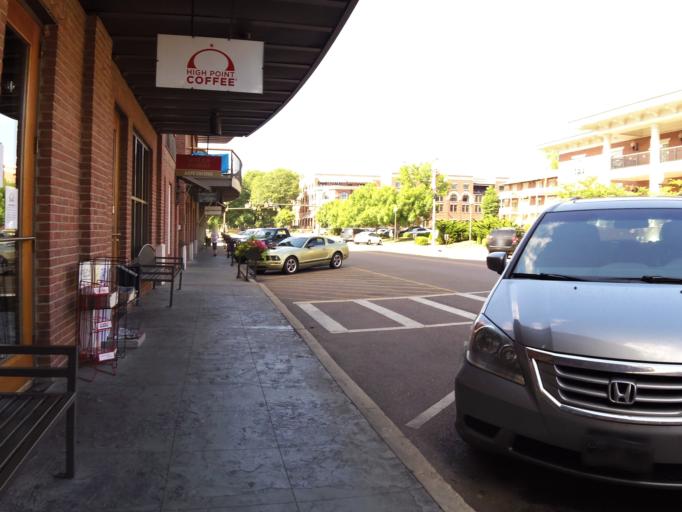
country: US
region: Mississippi
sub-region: Lafayette County
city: Oxford
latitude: 34.3676
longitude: -89.5186
